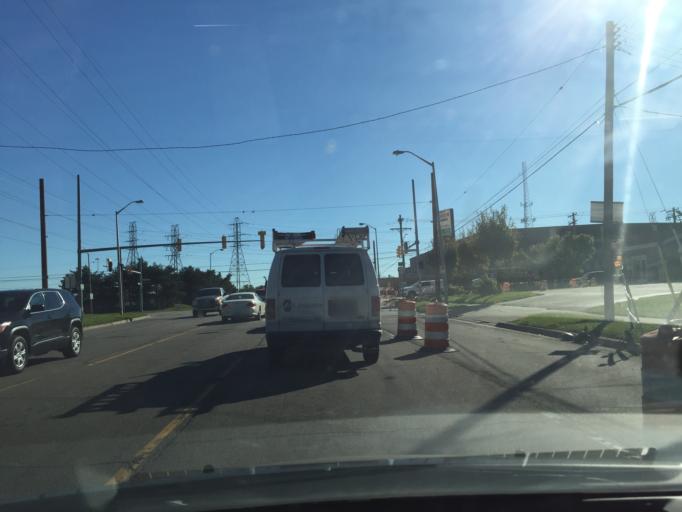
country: US
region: Michigan
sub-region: Oakland County
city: Pontiac
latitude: 42.6205
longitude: -83.2684
